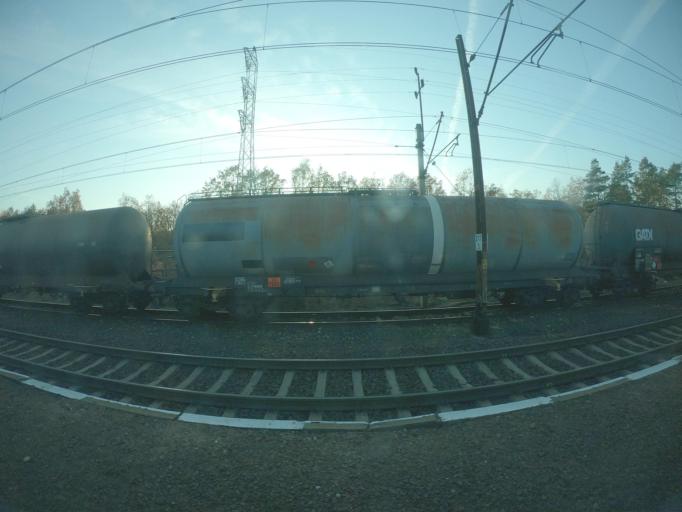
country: PL
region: Lubusz
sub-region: Powiat slubicki
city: Rzepin
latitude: 52.3068
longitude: 14.8672
